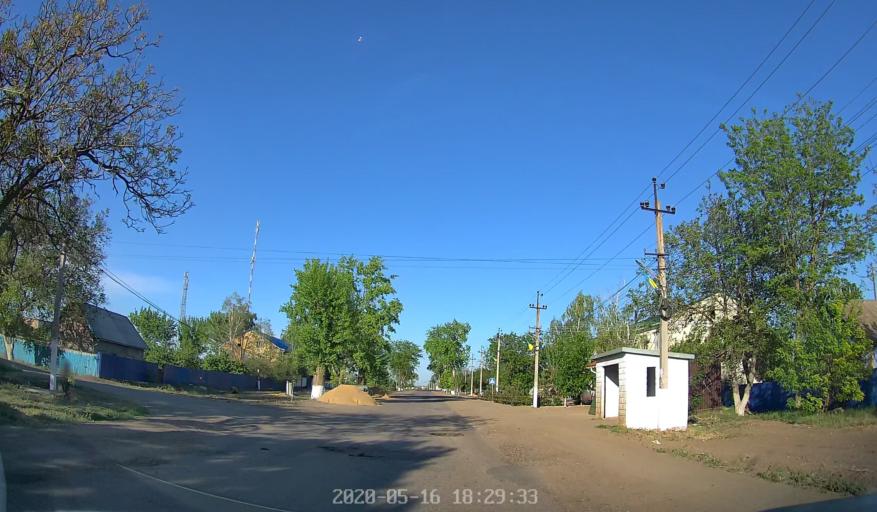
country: MD
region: Telenesti
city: Dnestrovsc
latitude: 46.5366
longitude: 30.0208
